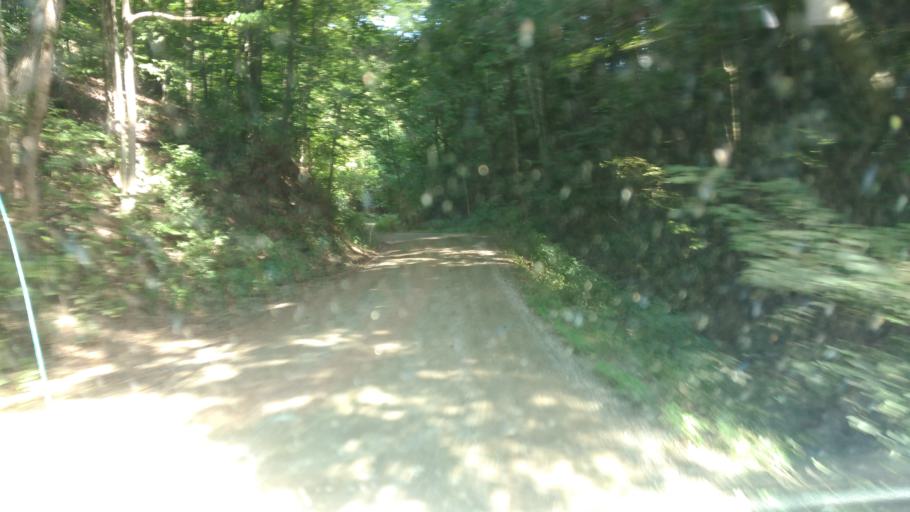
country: US
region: Ohio
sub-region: Holmes County
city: Millersburg
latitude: 40.6487
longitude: -81.8991
